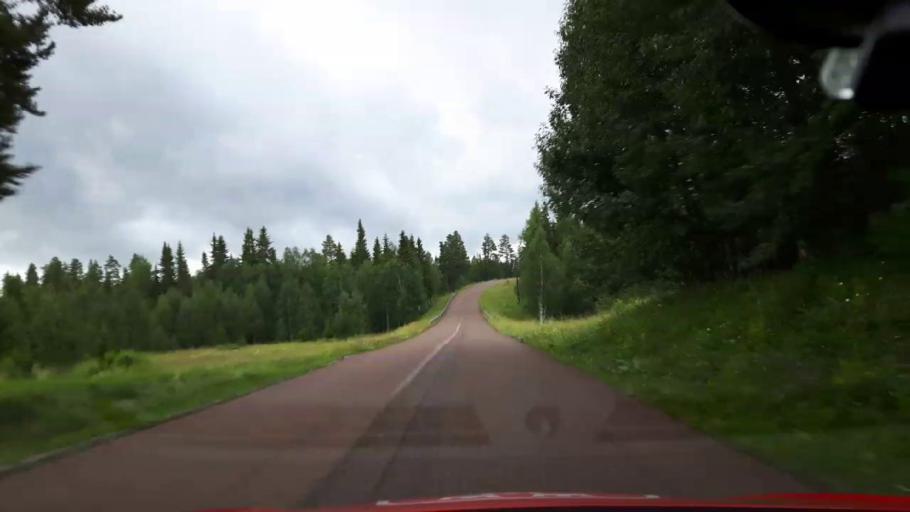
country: SE
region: Jaemtland
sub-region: Krokoms Kommun
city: Valla
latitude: 63.3471
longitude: 13.7224
